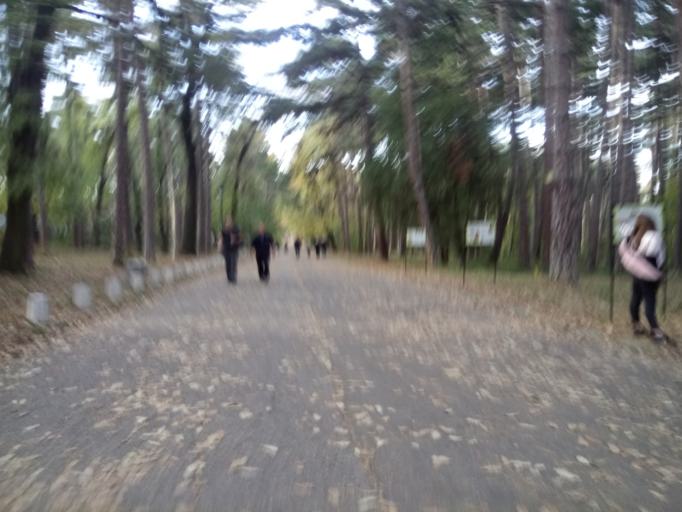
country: BG
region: Sofia-Capital
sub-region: Stolichna Obshtina
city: Sofia
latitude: 42.6825
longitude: 23.3443
